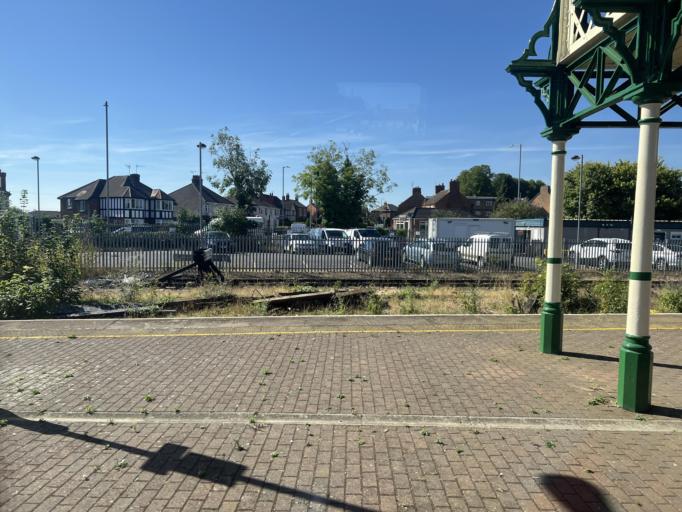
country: GB
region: England
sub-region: Lincolnshire
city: Sleaford
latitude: 52.9954
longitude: -0.4099
